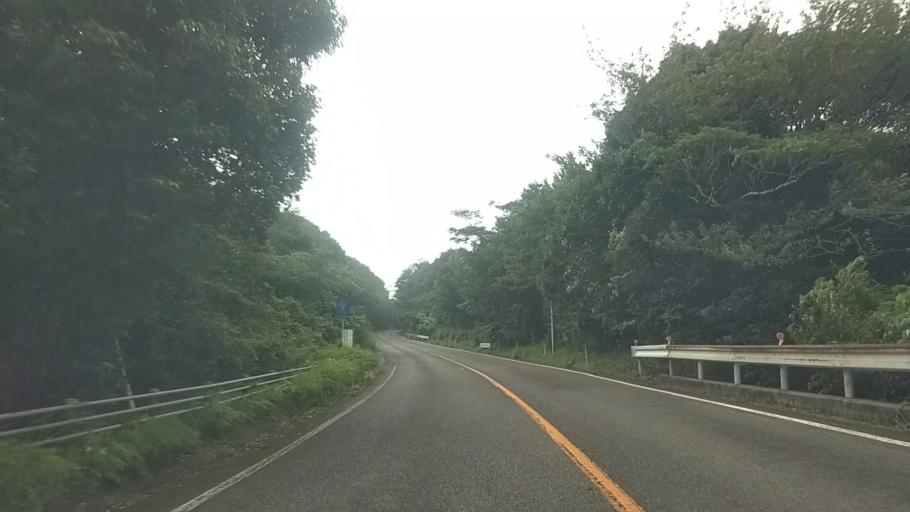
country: JP
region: Chiba
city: Kawaguchi
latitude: 35.2306
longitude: 140.0306
